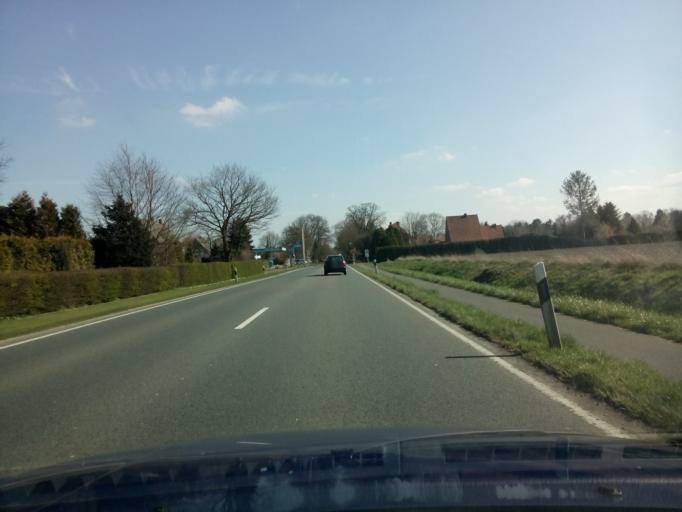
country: DE
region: Lower Saxony
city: Emlichheim
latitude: 52.6079
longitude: 6.8369
